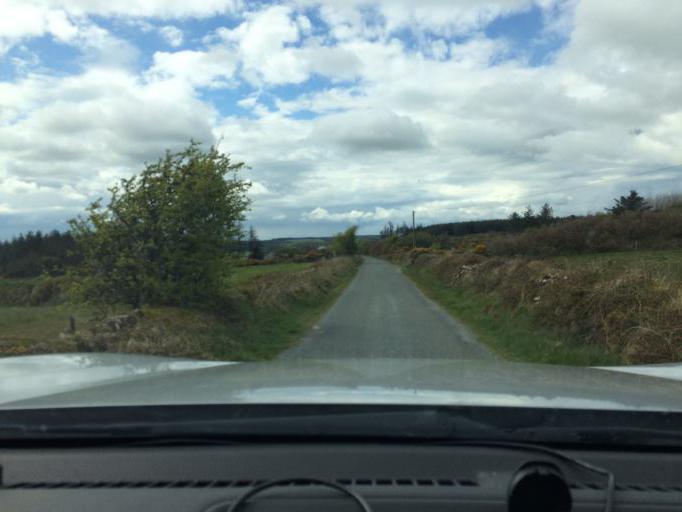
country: IE
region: Munster
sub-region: Waterford
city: Dungarvan
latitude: 52.0406
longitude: -7.6337
